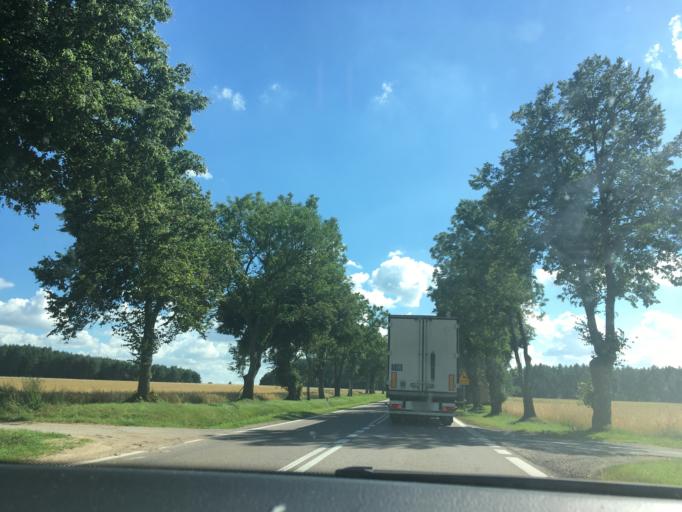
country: PL
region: Podlasie
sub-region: Powiat sokolski
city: Suchowola
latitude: 53.6031
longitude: 23.1145
